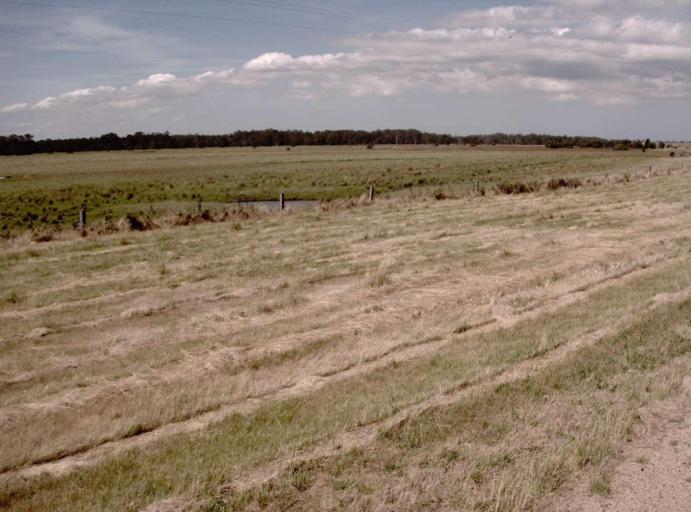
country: AU
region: Victoria
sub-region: Wellington
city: Sale
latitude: -38.1626
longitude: 146.9375
